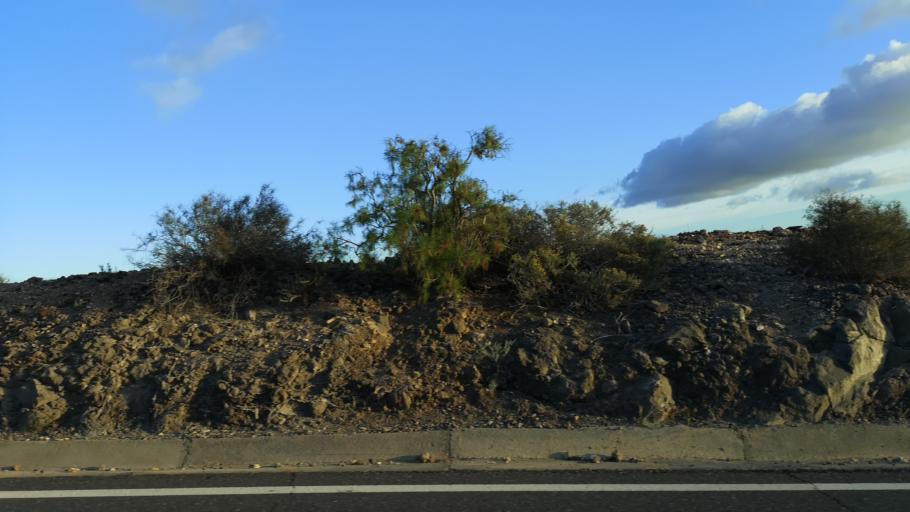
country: ES
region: Canary Islands
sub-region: Provincia de Santa Cruz de Tenerife
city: Alajero
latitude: 28.0287
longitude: -17.2064
